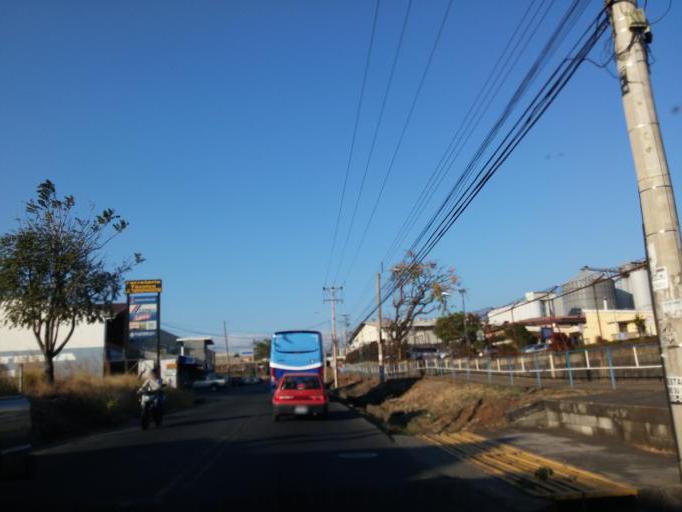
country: CR
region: Alajuela
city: Alajuela
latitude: 10.0075
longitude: -84.2177
